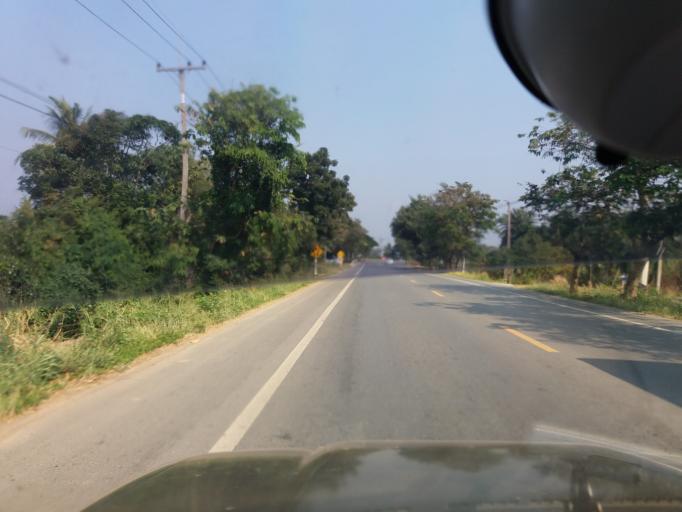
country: TH
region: Sing Buri
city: Sing Buri
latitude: 14.8859
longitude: 100.3698
